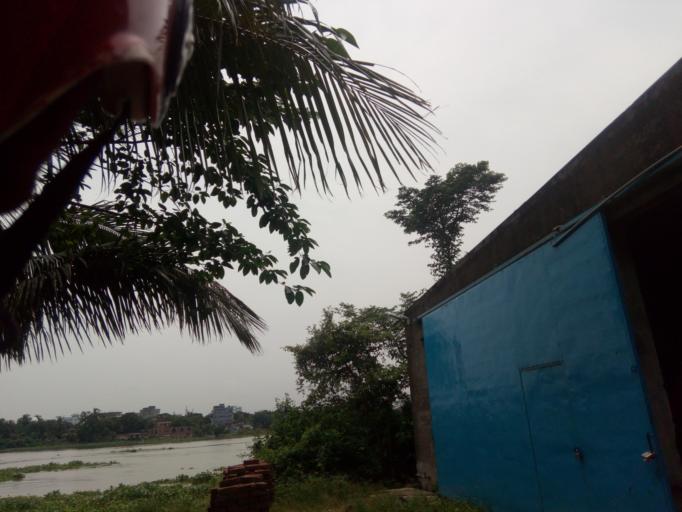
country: BD
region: Dhaka
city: Azimpur
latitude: 23.7413
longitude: 90.3497
